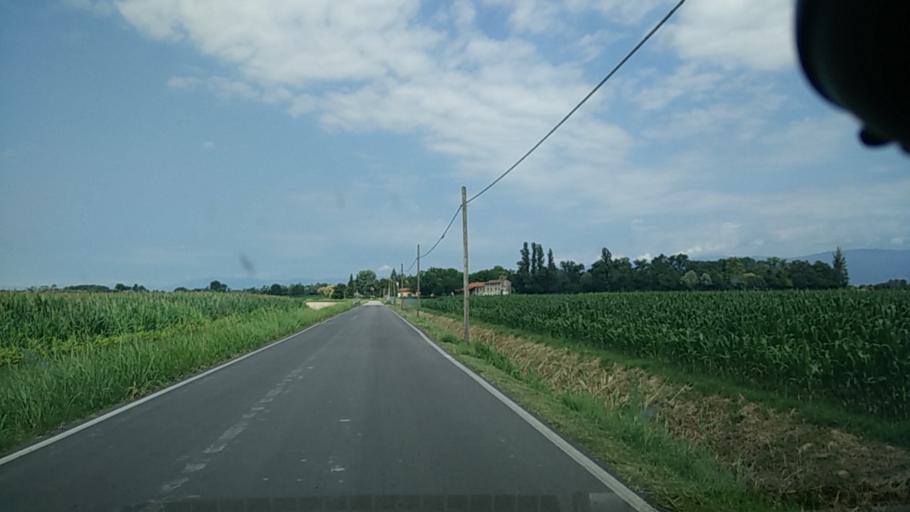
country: IT
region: Friuli Venezia Giulia
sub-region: Provincia di Pordenone
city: Puia-Villanova
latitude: 45.8308
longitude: 12.5819
